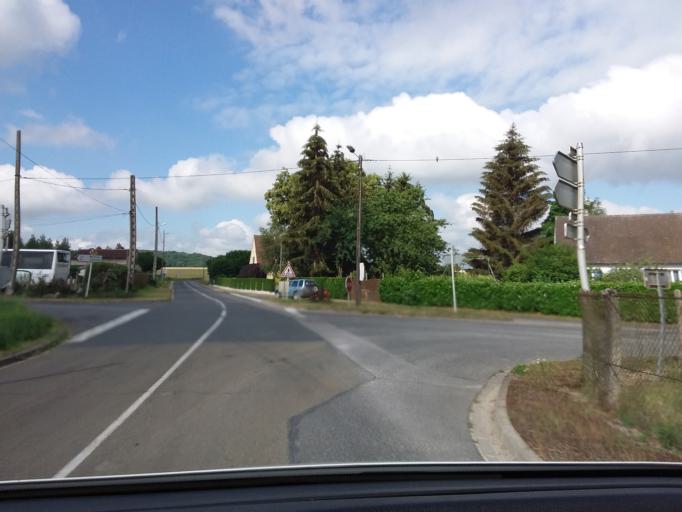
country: FR
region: Champagne-Ardenne
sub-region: Departement de la Marne
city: Fismes
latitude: 49.3778
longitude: 3.6856
